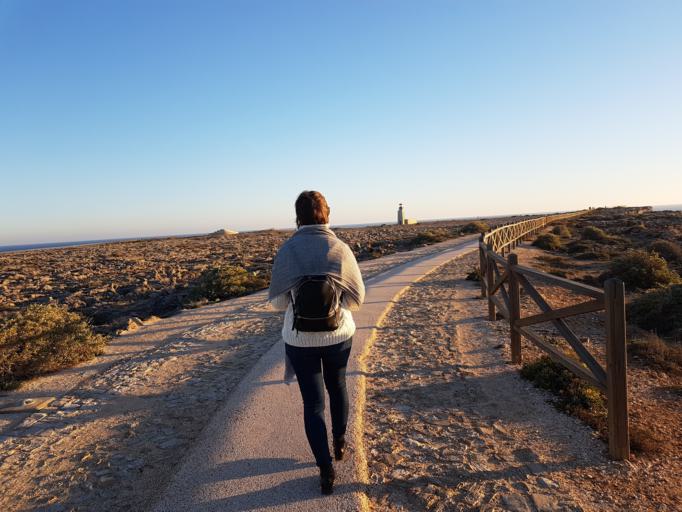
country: PT
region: Faro
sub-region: Vila do Bispo
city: Sagres
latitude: 36.9975
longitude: -8.9501
